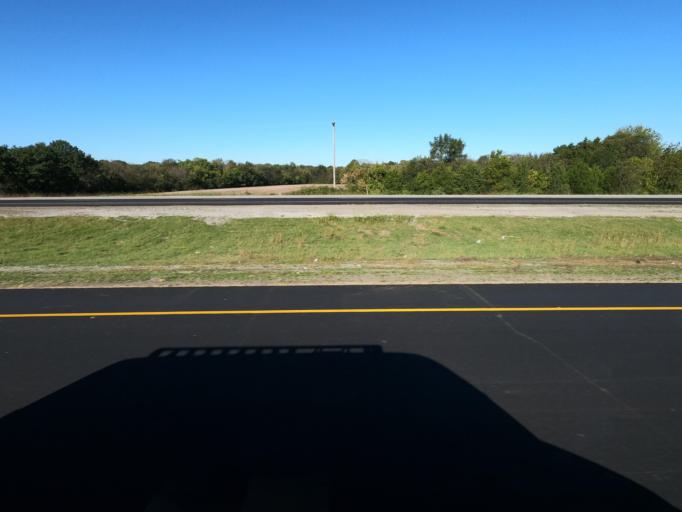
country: US
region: Tennessee
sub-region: Rutherford County
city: Smyrna
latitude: 35.9812
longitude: -86.4409
